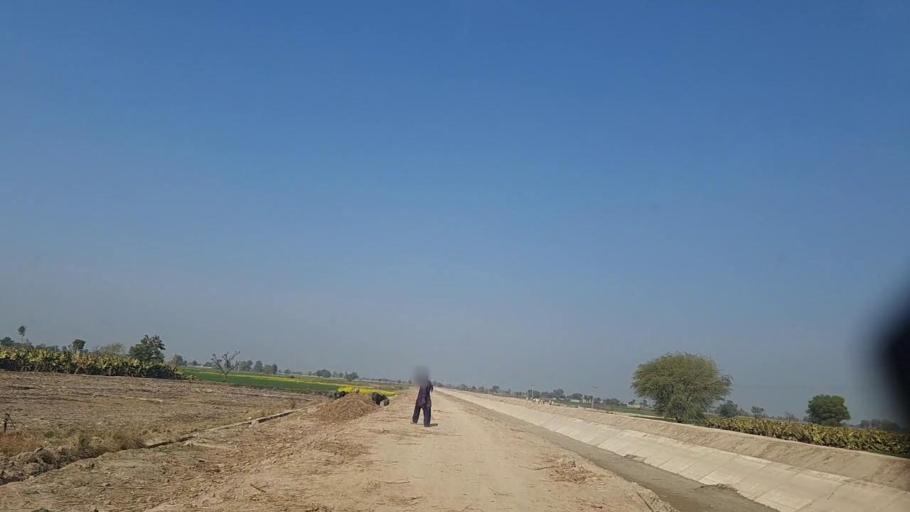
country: PK
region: Sindh
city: Sakrand
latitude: 26.1535
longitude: 68.3298
